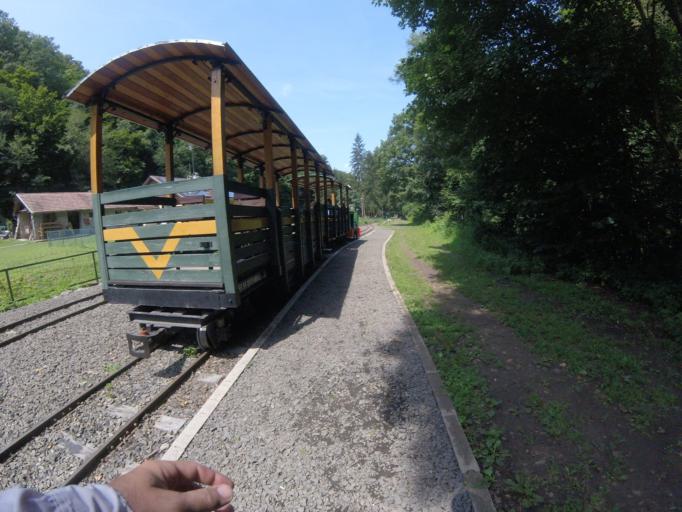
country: SK
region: Nitriansky
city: Sahy
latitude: 47.9815
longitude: 18.8965
